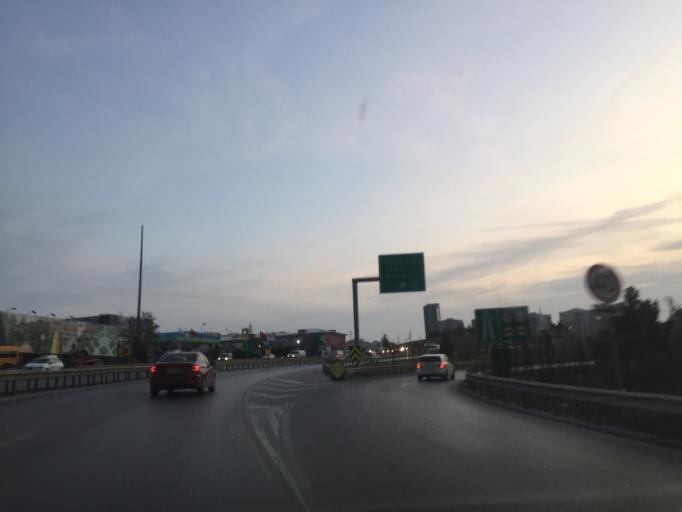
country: TR
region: Istanbul
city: Samandira
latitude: 40.9712
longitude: 29.2197
